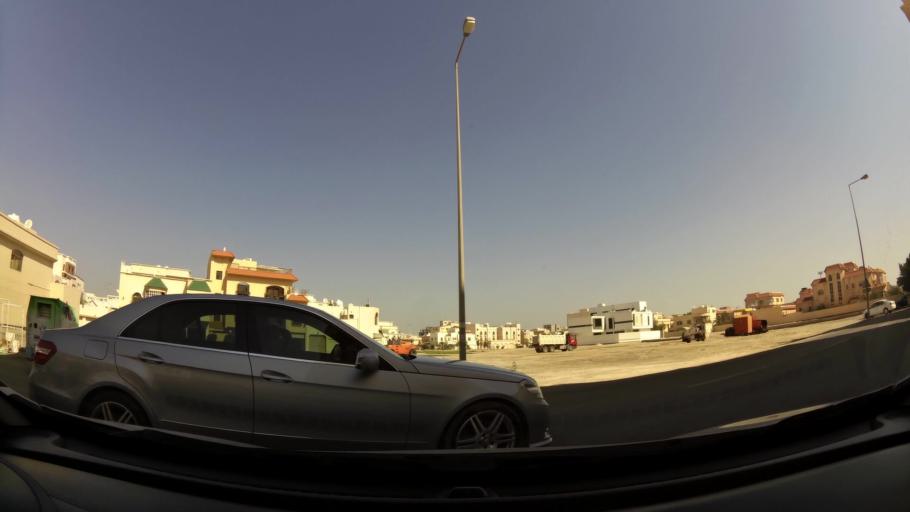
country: BH
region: Manama
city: Manama
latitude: 26.2116
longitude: 50.5788
